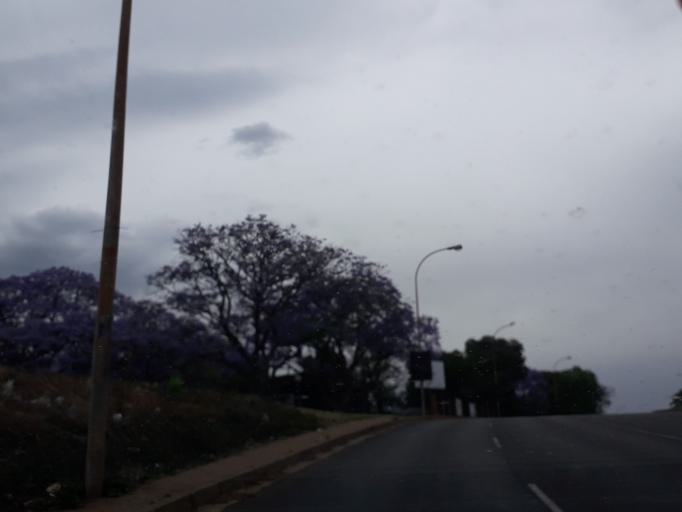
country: ZA
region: Gauteng
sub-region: City of Johannesburg Metropolitan Municipality
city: Johannesburg
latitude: -26.1804
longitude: 28.0453
